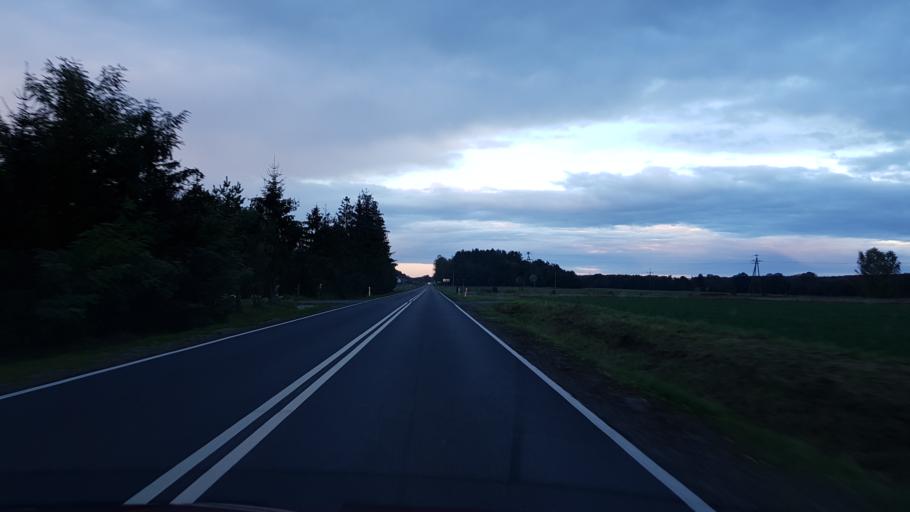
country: PL
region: Greater Poland Voivodeship
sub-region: Powiat zlotowski
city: Krajenka
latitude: 53.2646
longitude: 16.9237
